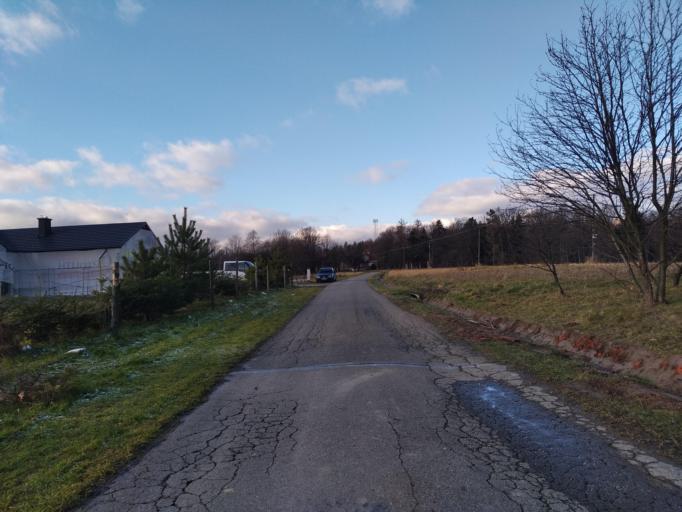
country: PL
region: Subcarpathian Voivodeship
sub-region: Powiat strzyzowski
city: Babica
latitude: 49.9463
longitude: 21.8757
